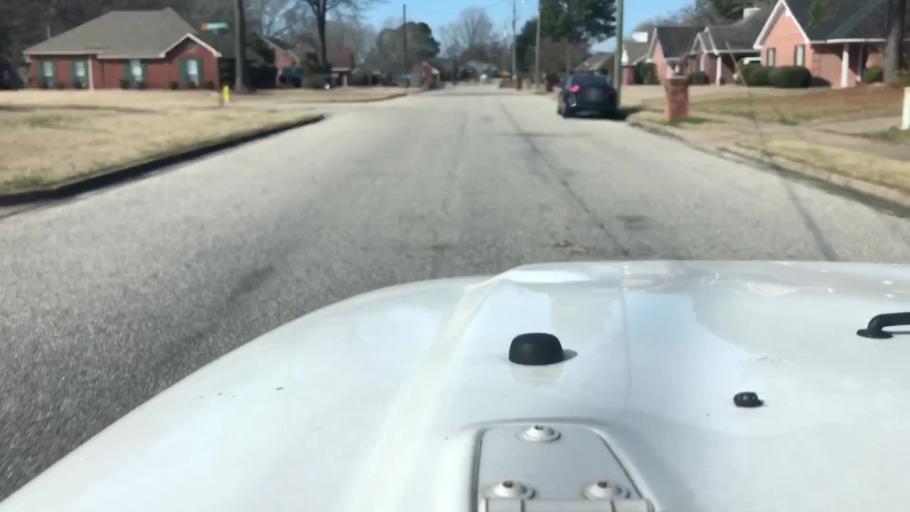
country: US
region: Alabama
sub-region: Elmore County
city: Blue Ridge
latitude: 32.4072
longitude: -86.1918
